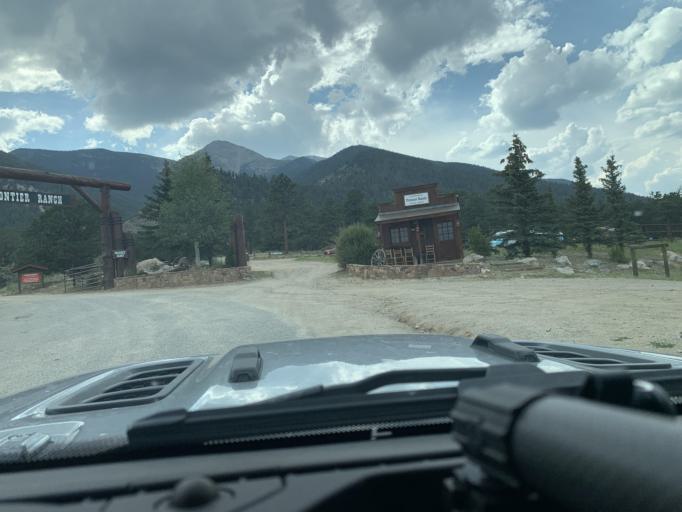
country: US
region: Colorado
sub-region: Chaffee County
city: Buena Vista
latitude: 38.7399
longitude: -106.1750
